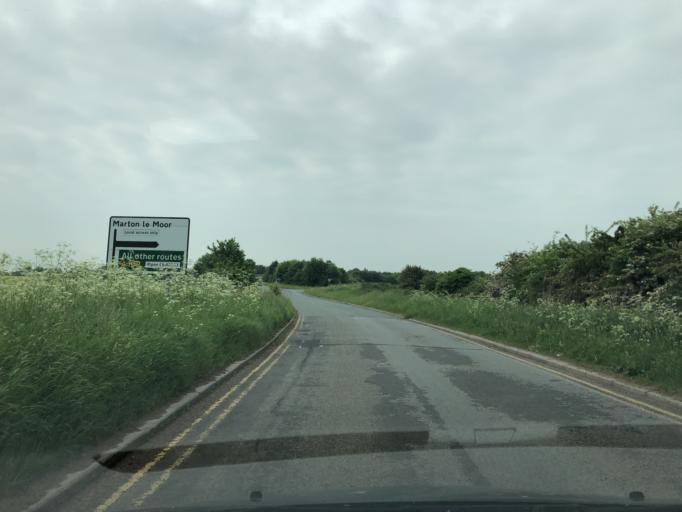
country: GB
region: England
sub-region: North Yorkshire
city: Boroughbridge
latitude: 54.1265
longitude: -1.4097
